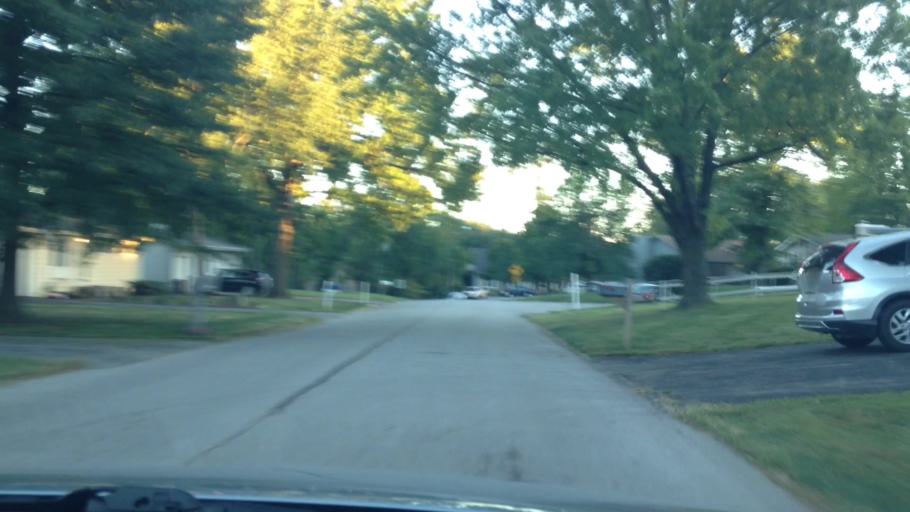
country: US
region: Missouri
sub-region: Platte County
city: Parkville
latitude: 39.2187
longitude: -94.6584
